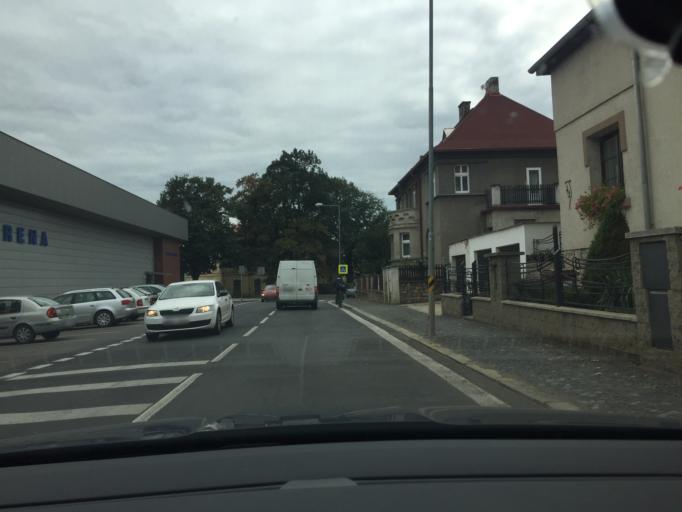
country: CZ
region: Ustecky
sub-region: Okres Litomerice
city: Litomerice
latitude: 50.5337
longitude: 14.1231
